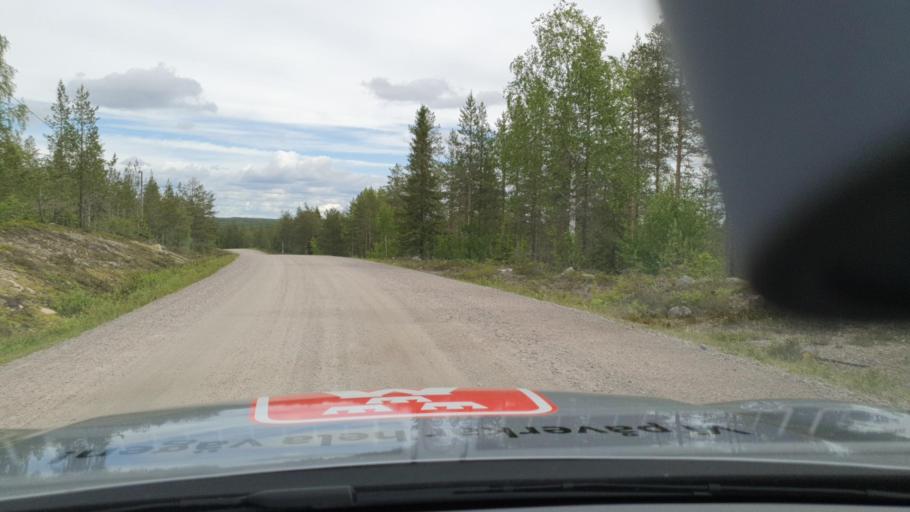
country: SE
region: Norrbotten
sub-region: Kalix Kommun
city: Kalix
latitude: 65.9297
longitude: 23.5237
